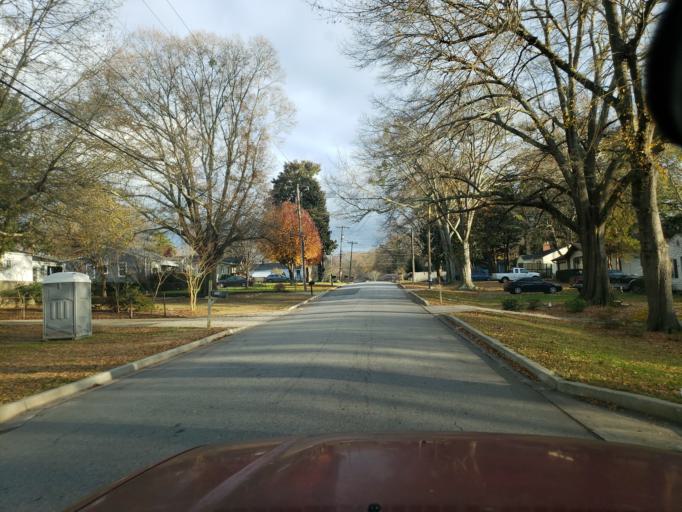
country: US
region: South Carolina
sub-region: Greenville County
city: Greenville
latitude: 34.8323
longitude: -82.3622
